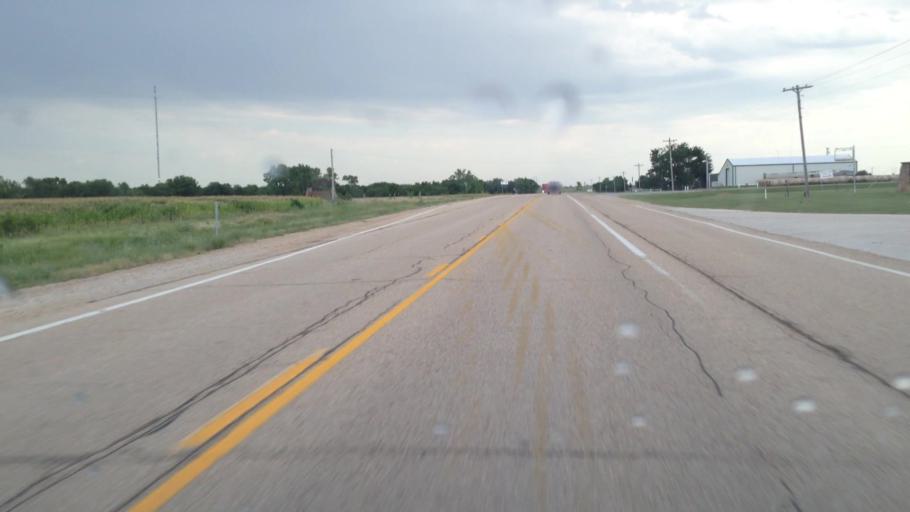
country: US
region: Kansas
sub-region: Coffey County
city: Burlington
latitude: 38.1716
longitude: -95.7389
